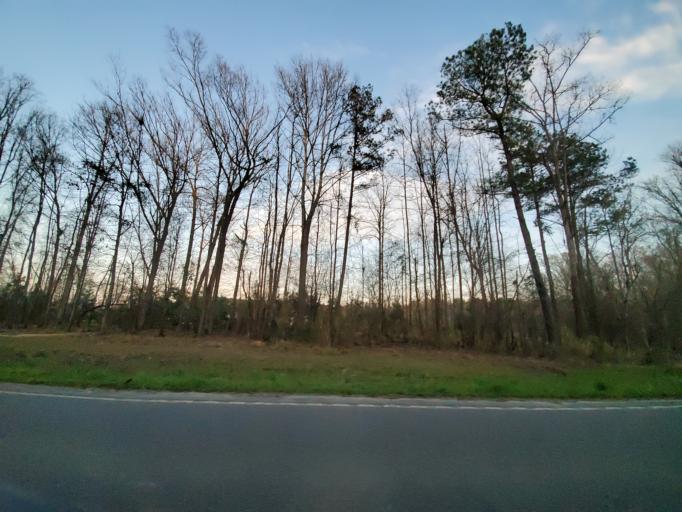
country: US
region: South Carolina
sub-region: Dorchester County
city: Ridgeville
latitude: 32.9823
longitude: -80.3063
